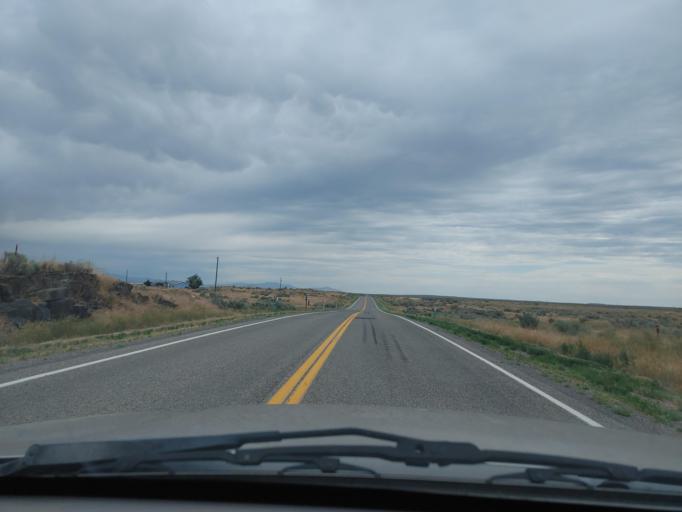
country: US
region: Idaho
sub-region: Lincoln County
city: Shoshone
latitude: 43.0548
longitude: -114.1359
